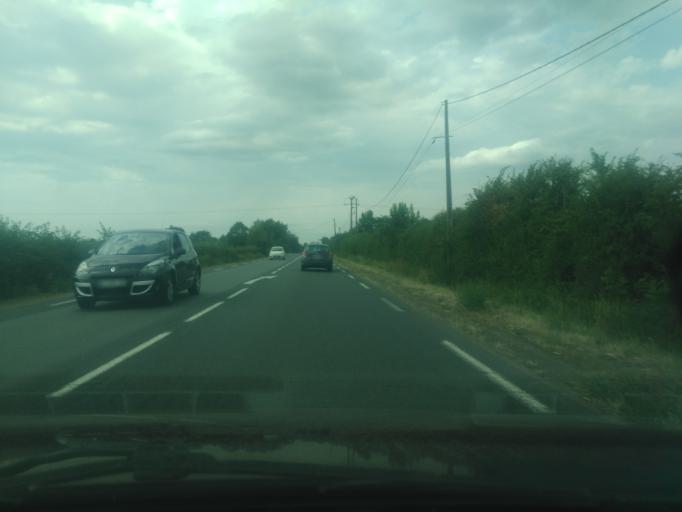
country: FR
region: Pays de la Loire
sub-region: Departement de la Vendee
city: Sainte-Cecile
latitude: 46.7463
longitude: -1.0910
